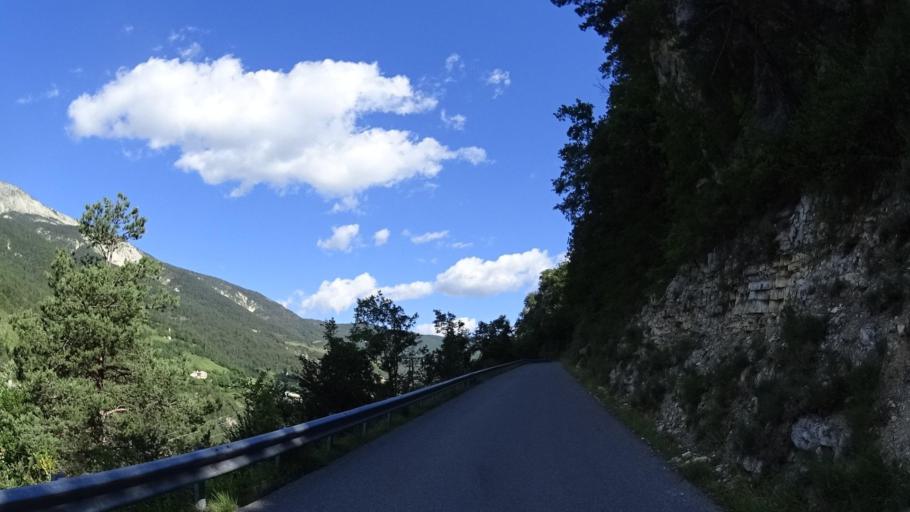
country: FR
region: Provence-Alpes-Cote d'Azur
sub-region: Departement des Alpes-de-Haute-Provence
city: Annot
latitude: 44.0154
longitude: 6.6349
